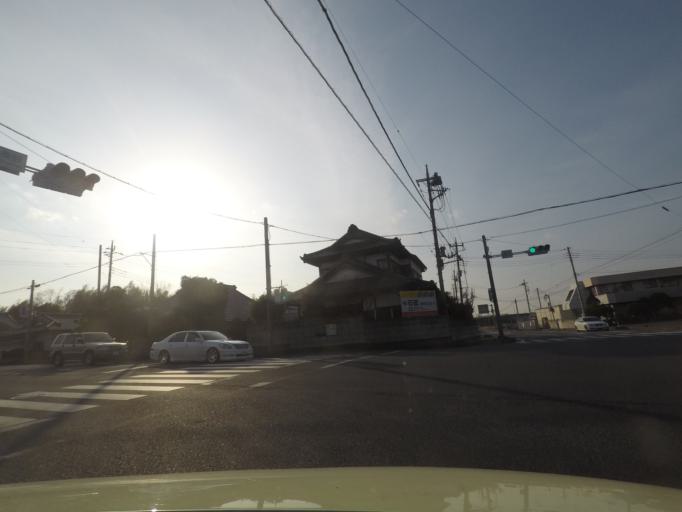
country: JP
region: Ibaraki
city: Okunoya
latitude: 36.2866
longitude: 140.4219
